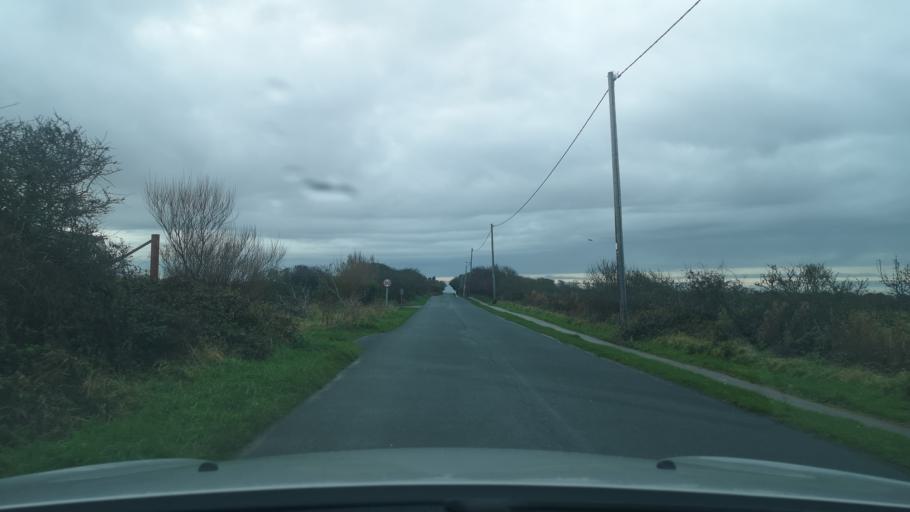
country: GB
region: England
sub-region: East Riding of Yorkshire
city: Easington
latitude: 53.6200
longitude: 0.1372
